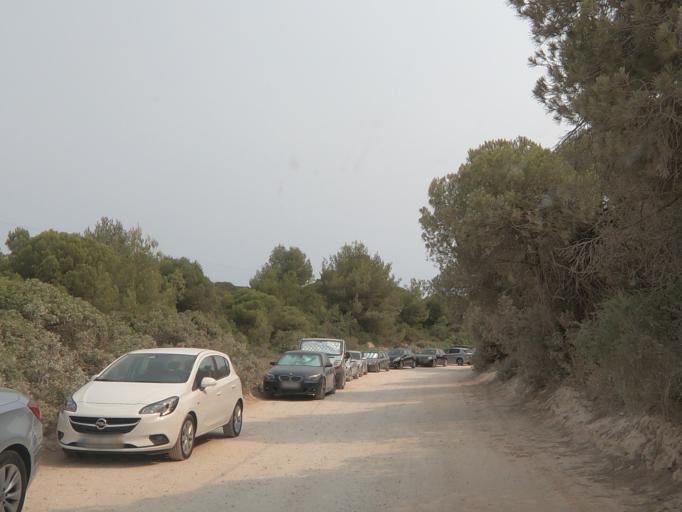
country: PT
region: Faro
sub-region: Silves
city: Armacao de Pera
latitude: 37.0925
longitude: -8.4002
